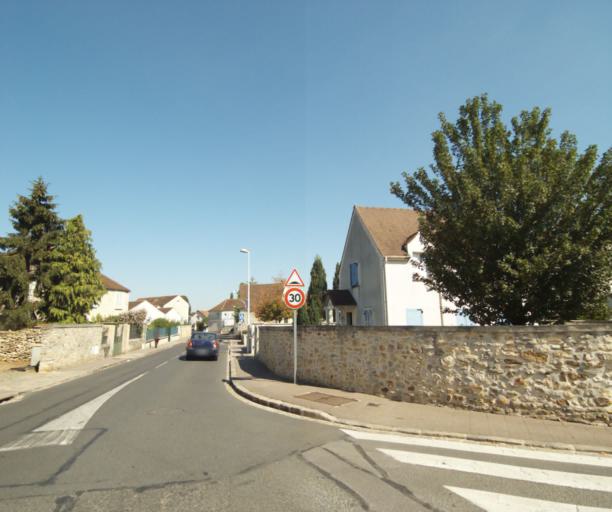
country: FR
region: Ile-de-France
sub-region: Departement de Seine-et-Marne
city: Moissy-Cramayel
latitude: 48.6267
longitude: 2.5953
